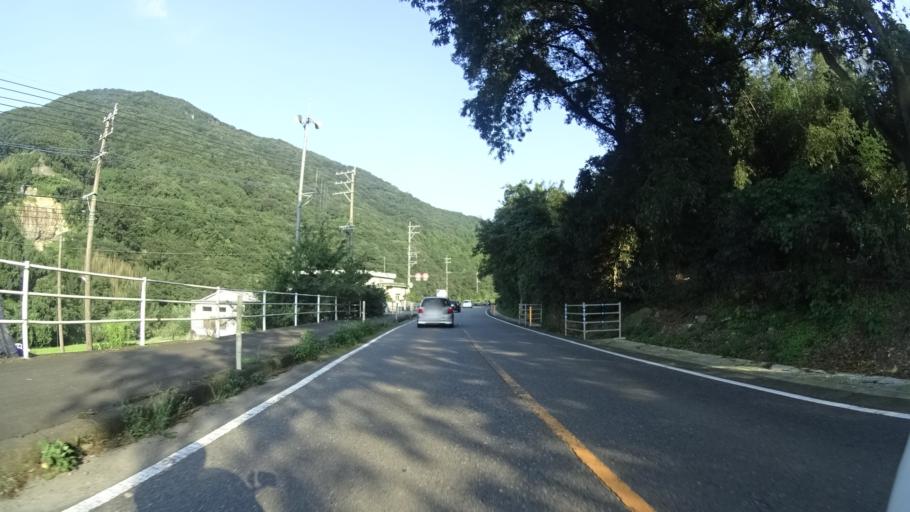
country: JP
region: Oita
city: Bungo-Takada-shi
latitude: 33.4902
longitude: 131.3309
